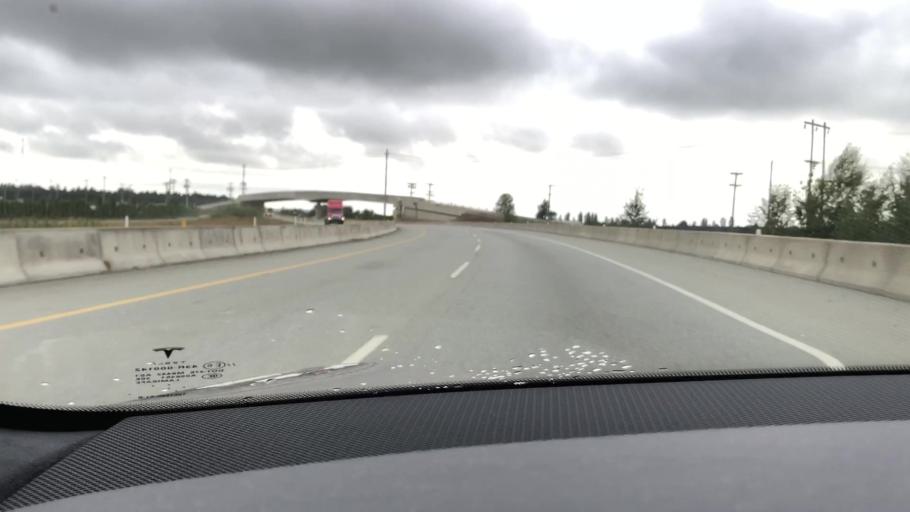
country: CA
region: British Columbia
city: Ladner
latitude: 49.1257
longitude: -123.0227
